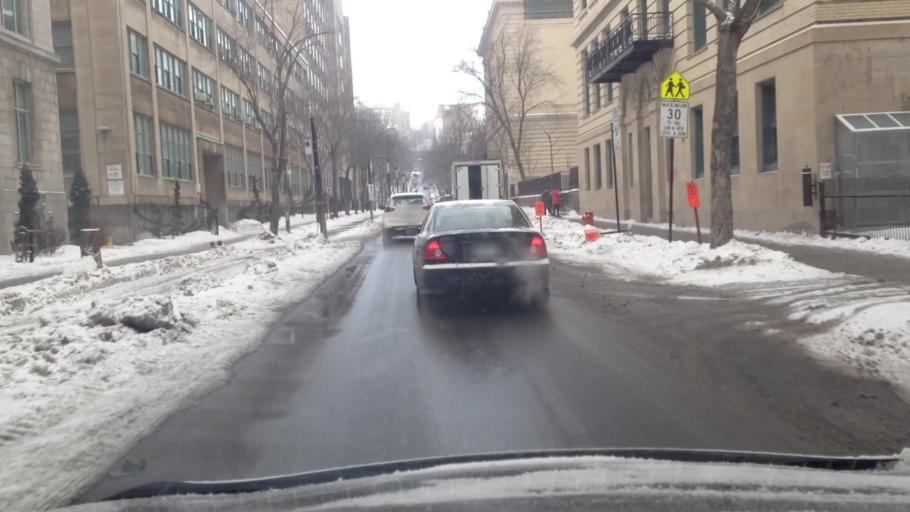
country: CA
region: Quebec
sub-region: Montreal
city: Montreal
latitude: 45.5055
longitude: -73.5745
